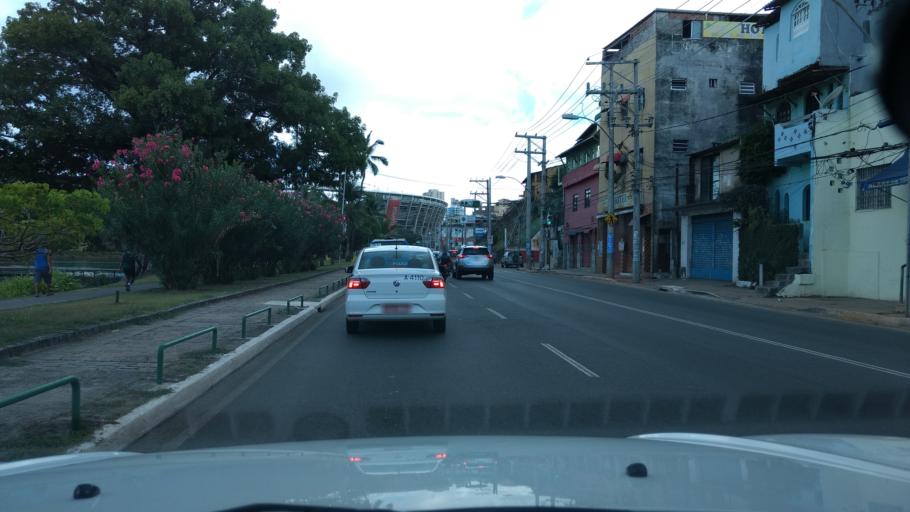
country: BR
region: Bahia
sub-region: Salvador
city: Salvador
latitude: -12.9843
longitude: -38.5039
